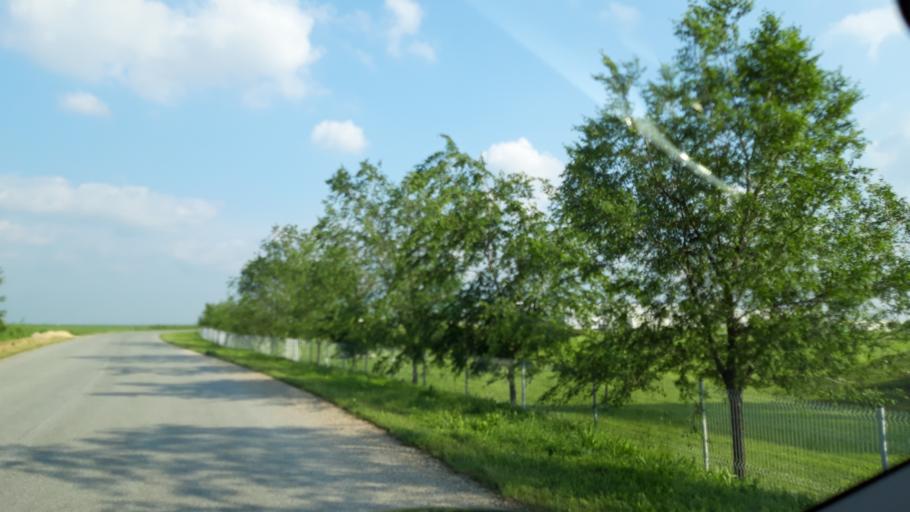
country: RS
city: Beska
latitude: 45.0963
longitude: 20.0932
